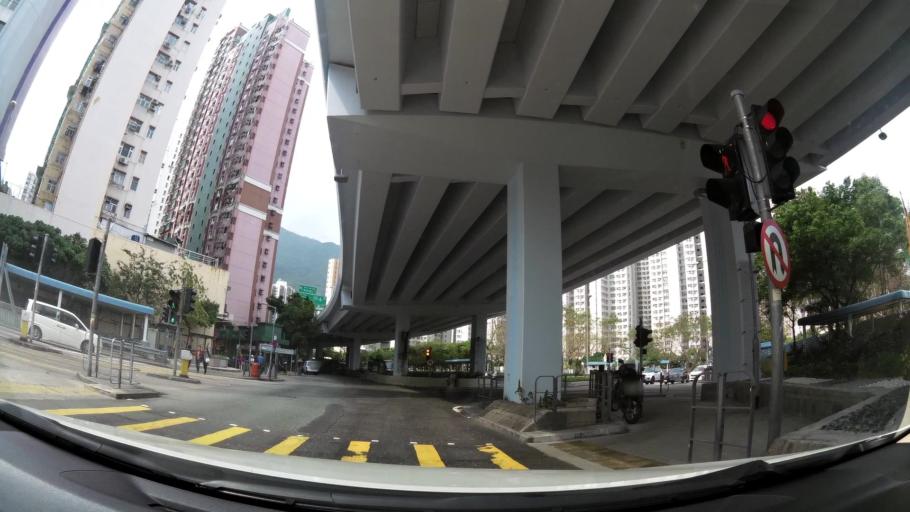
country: HK
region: Wanchai
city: Wan Chai
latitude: 22.2819
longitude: 114.2308
